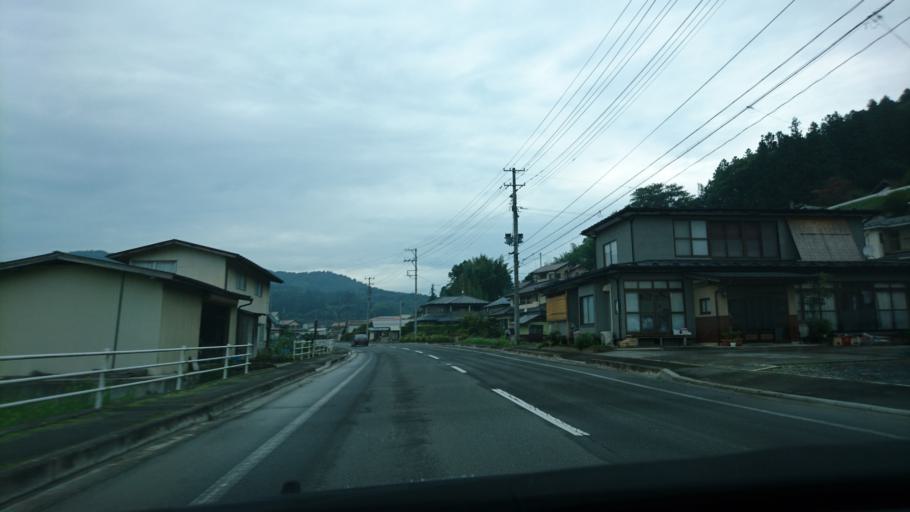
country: JP
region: Iwate
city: Ichinoseki
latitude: 38.9739
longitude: 141.2433
